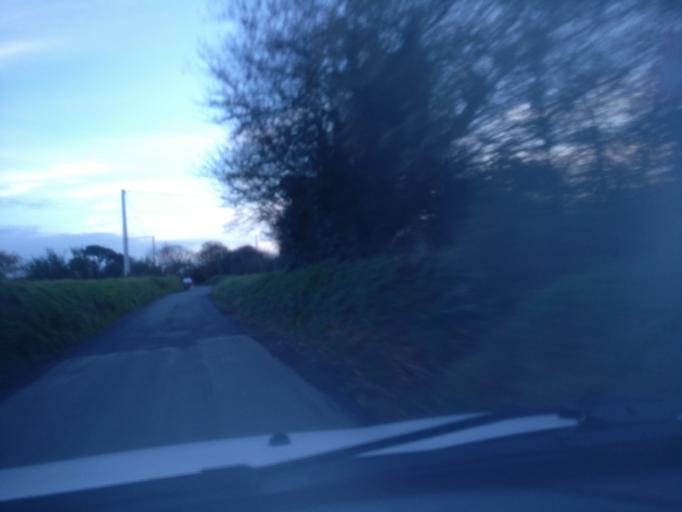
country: FR
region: Brittany
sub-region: Departement des Cotes-d'Armor
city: Saint-Quay-Perros
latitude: 48.8000
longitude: -3.4615
